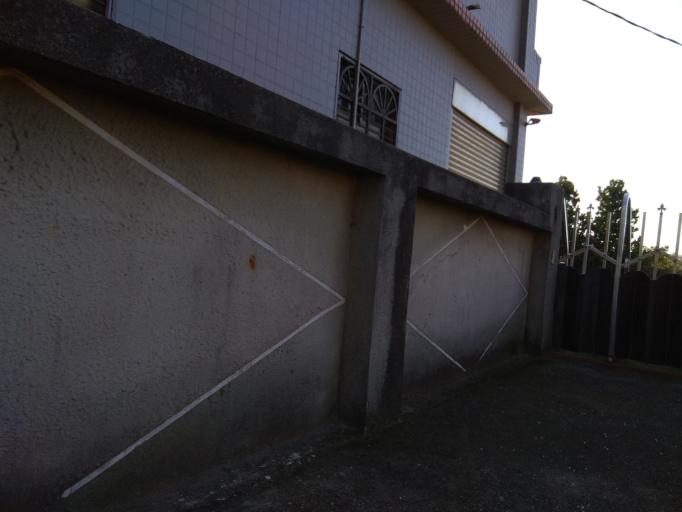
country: TW
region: Taiwan
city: Taoyuan City
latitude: 24.9931
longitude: 121.1987
